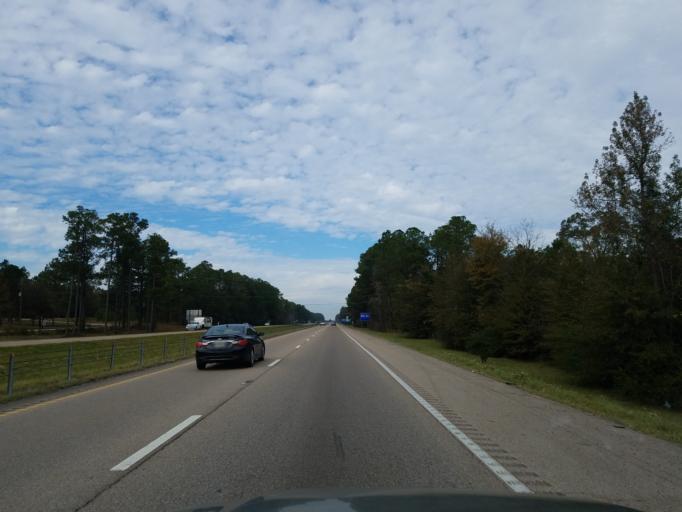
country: US
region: Mississippi
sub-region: Lamar County
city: West Hattiesburg
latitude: 31.2494
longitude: -89.3296
